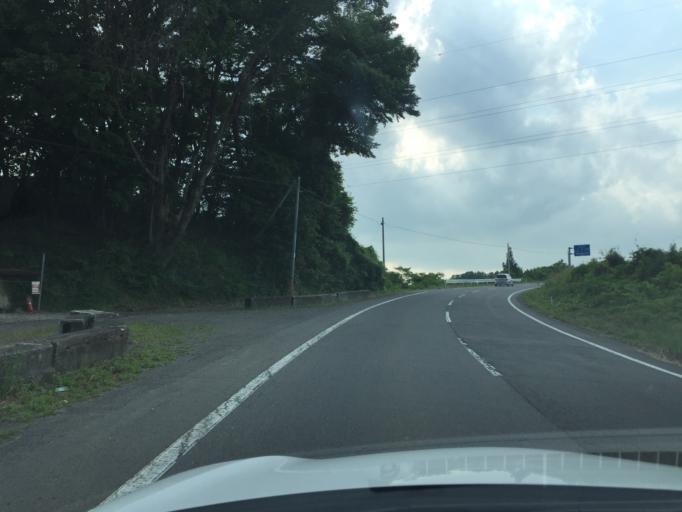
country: JP
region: Fukushima
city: Miharu
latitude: 37.3973
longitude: 140.4485
